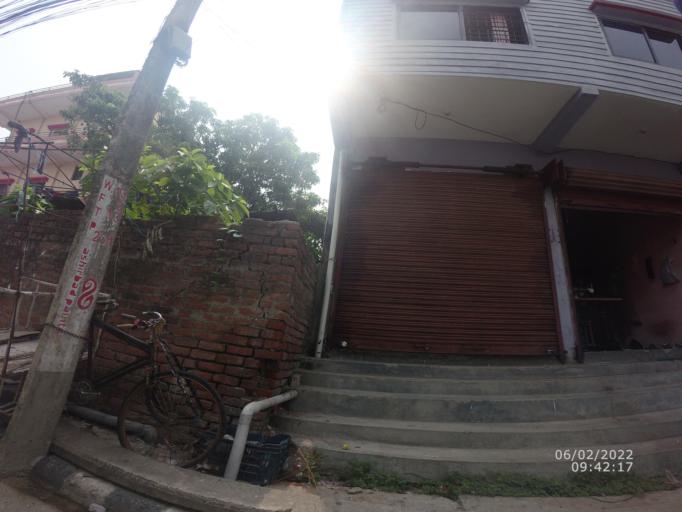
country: NP
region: Western Region
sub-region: Lumbini Zone
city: Bhairahawa
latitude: 27.5024
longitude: 83.4512
